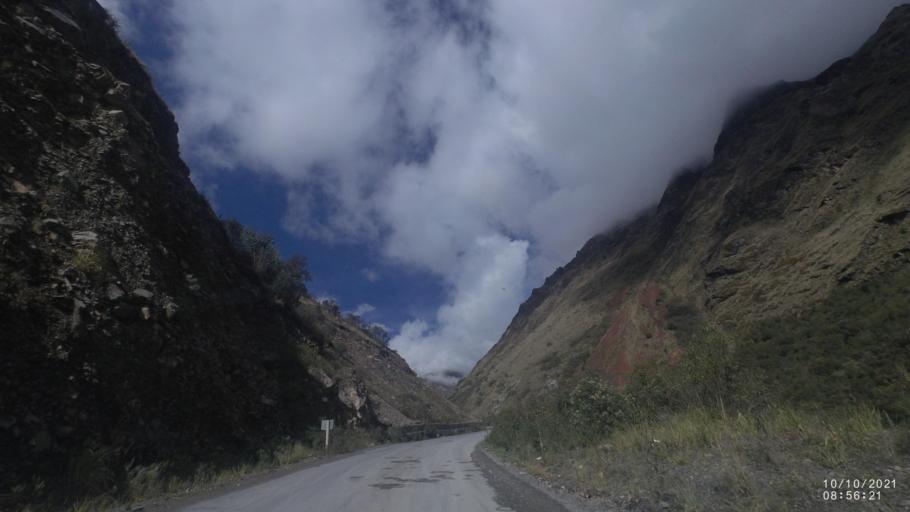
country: BO
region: La Paz
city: Quime
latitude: -16.9889
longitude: -67.2445
